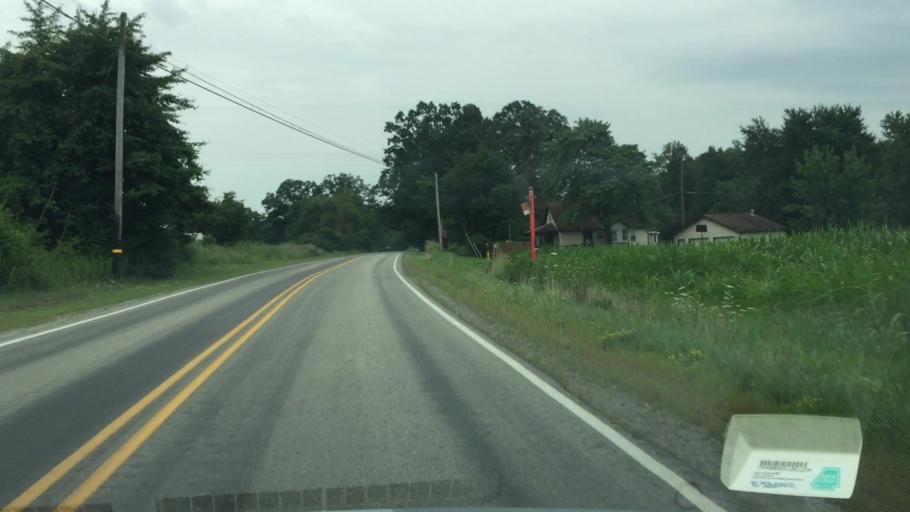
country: US
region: Pennsylvania
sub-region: Butler County
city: Saxonburg
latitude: 40.7129
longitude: -79.8523
